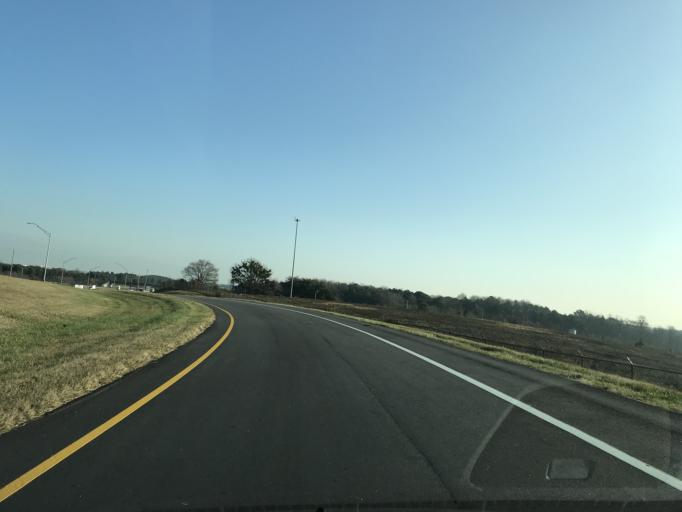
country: US
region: Georgia
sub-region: Fulton County
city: Hapeville
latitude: 33.6248
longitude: -84.4204
